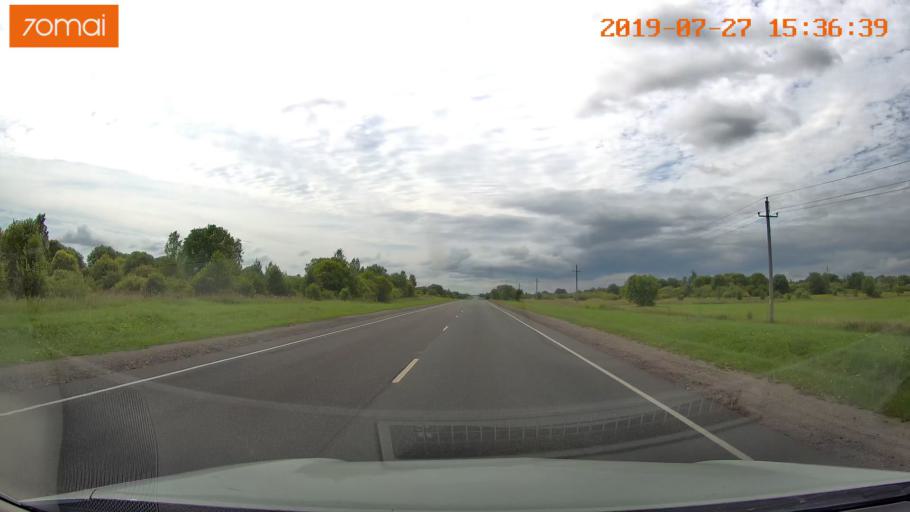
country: RU
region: Kaliningrad
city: Gusev
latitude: 54.6114
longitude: 22.3635
